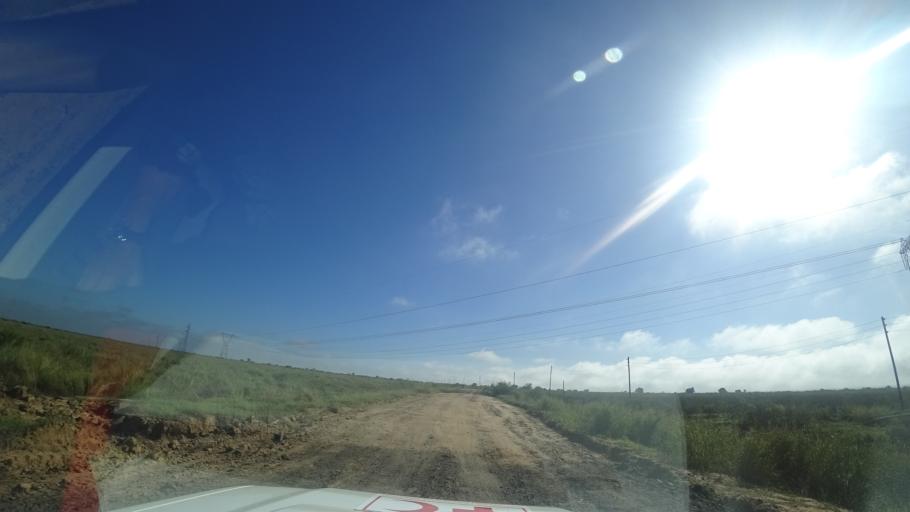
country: MZ
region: Sofala
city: Dondo
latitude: -19.4605
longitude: 34.5630
